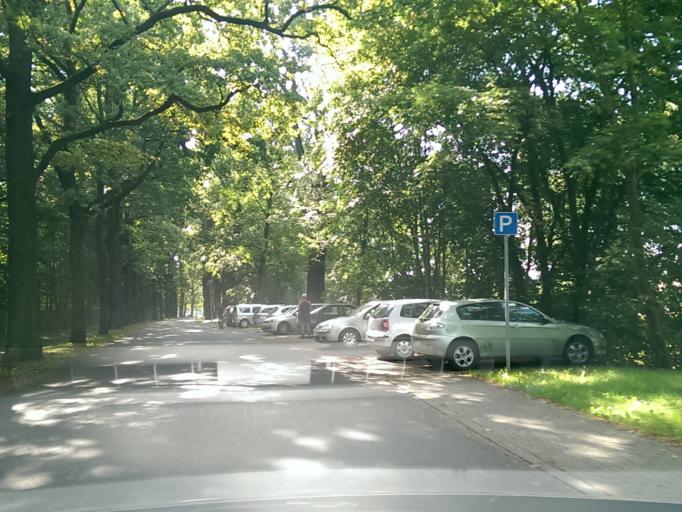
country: DE
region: Saxony
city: Zittau
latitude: 50.9036
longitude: 14.8275
